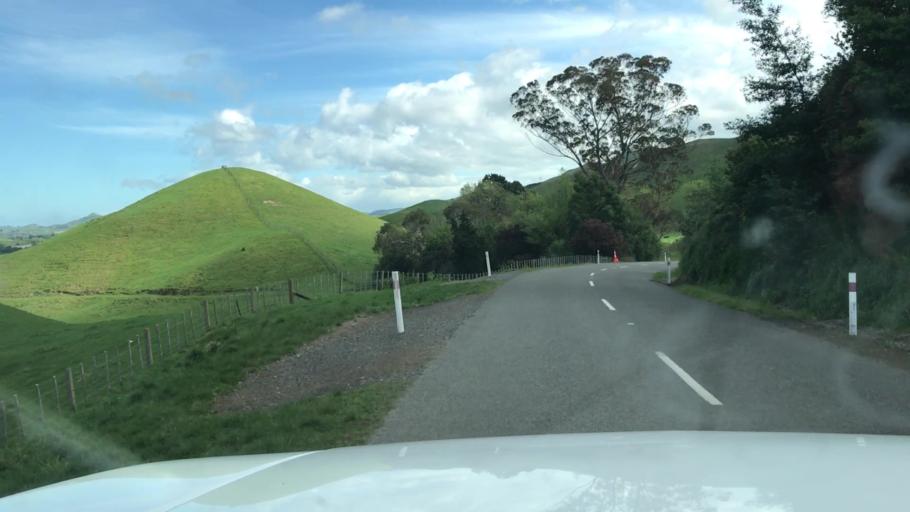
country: NZ
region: Hawke's Bay
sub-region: Hastings District
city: Hastings
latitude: -39.8184
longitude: 176.7423
